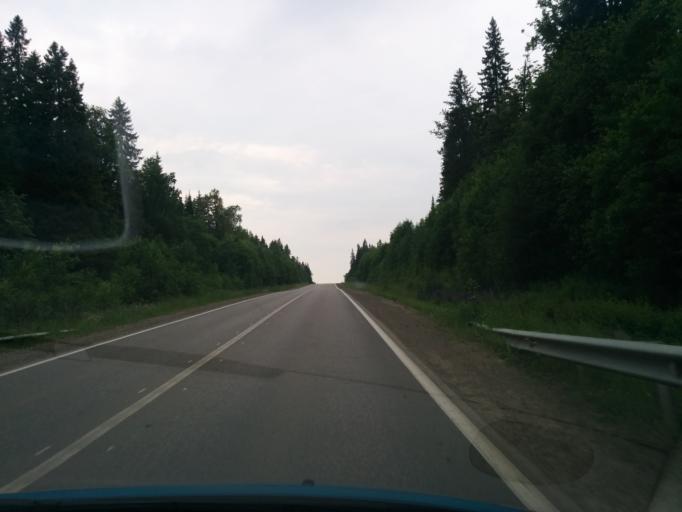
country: RU
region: Perm
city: Perm
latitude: 58.1917
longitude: 56.2143
